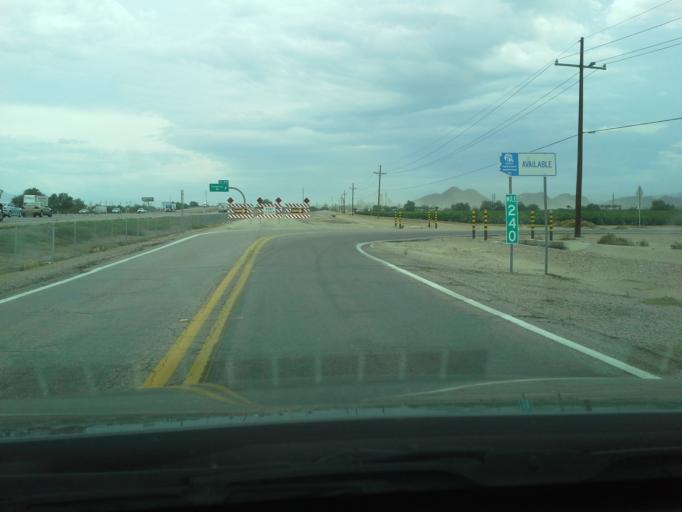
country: US
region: Arizona
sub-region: Pima County
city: Marana
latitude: 32.4286
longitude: -111.1700
